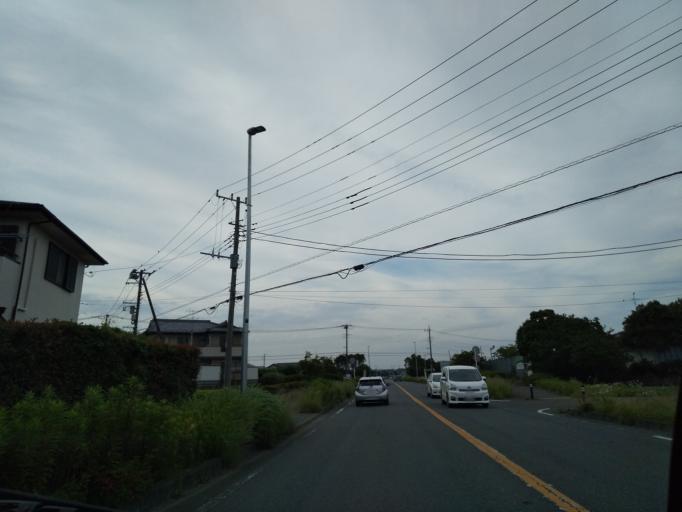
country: JP
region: Kanagawa
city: Atsugi
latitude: 35.4727
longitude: 139.3585
